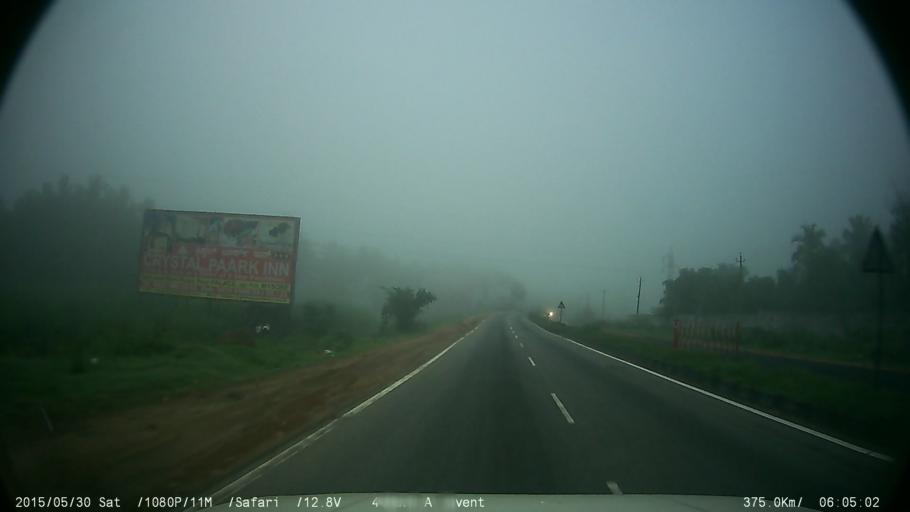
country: IN
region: Karnataka
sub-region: Mandya
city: Shrirangapattana
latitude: 12.3985
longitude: 76.6686
